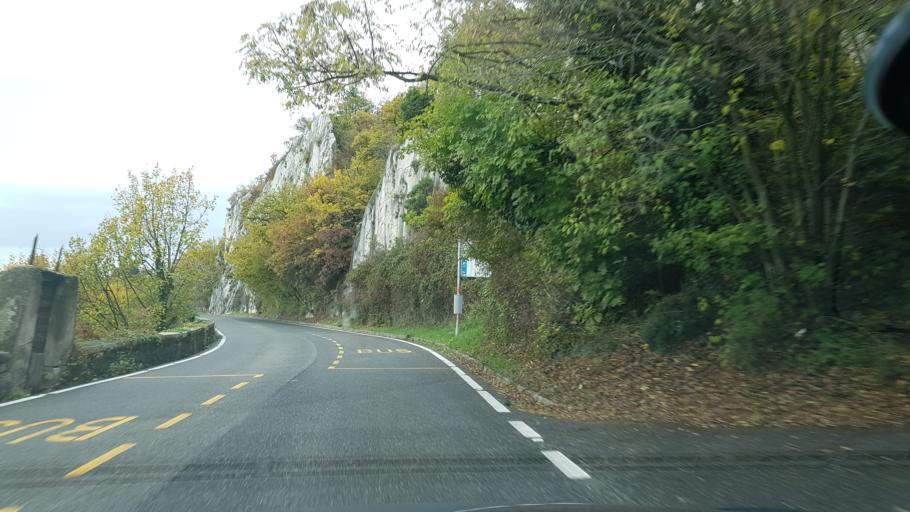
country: IT
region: Friuli Venezia Giulia
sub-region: Provincia di Trieste
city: Prosecco-Contovello
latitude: 45.6960
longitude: 13.7420
